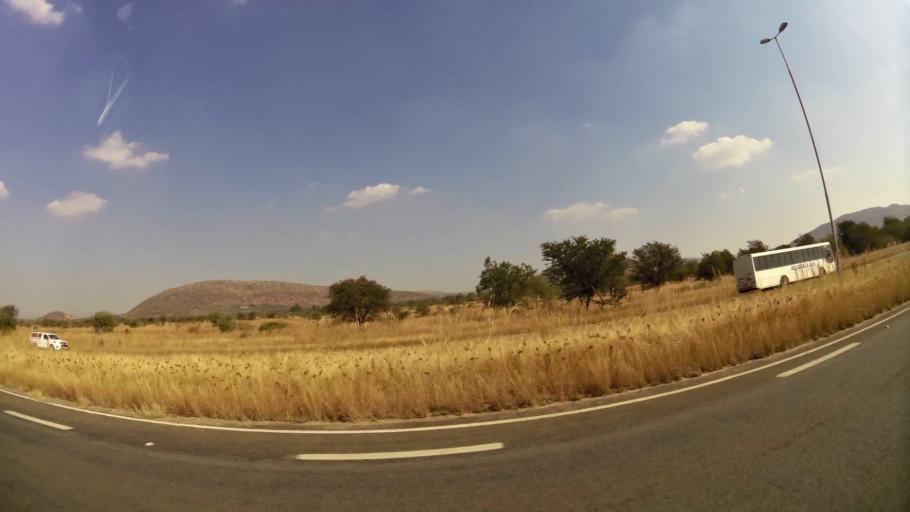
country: ZA
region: North-West
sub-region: Bojanala Platinum District Municipality
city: Rustenburg
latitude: -25.5536
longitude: 27.1378
